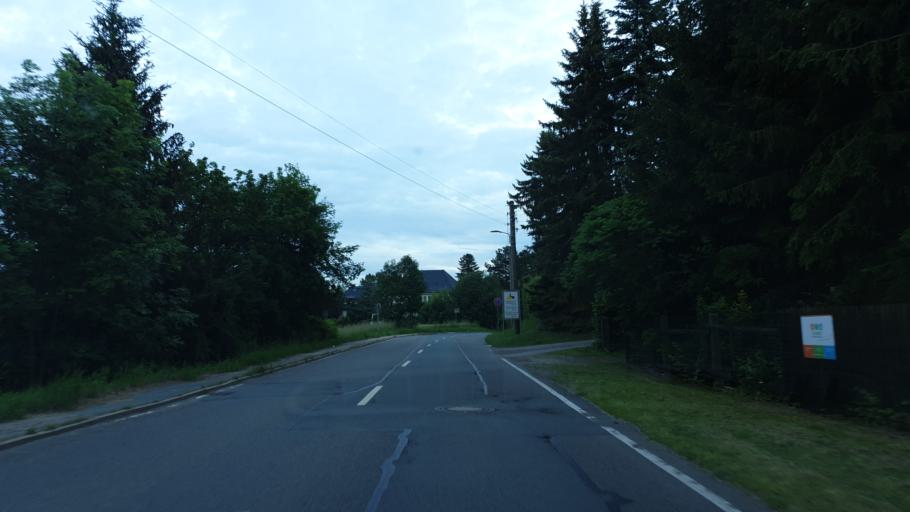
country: DE
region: Saxony
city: Hohenstein-Ernstthal
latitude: 50.7906
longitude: 12.7218
